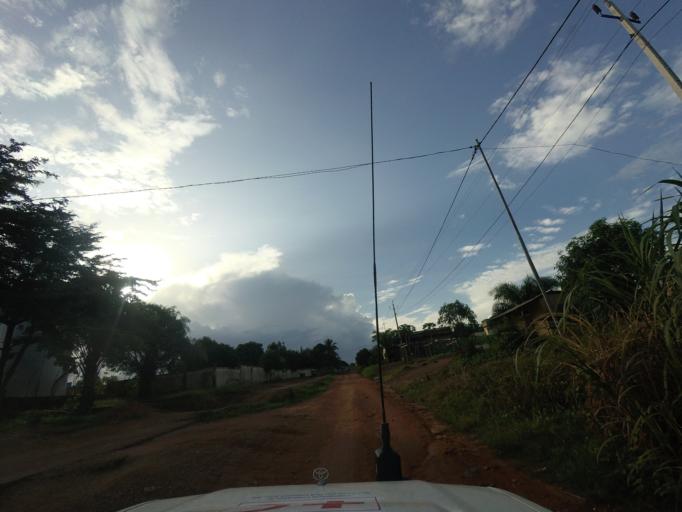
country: GN
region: Nzerekore
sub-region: Nzerekore Prefecture
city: Nzerekore
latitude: 7.7220
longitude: -8.8244
